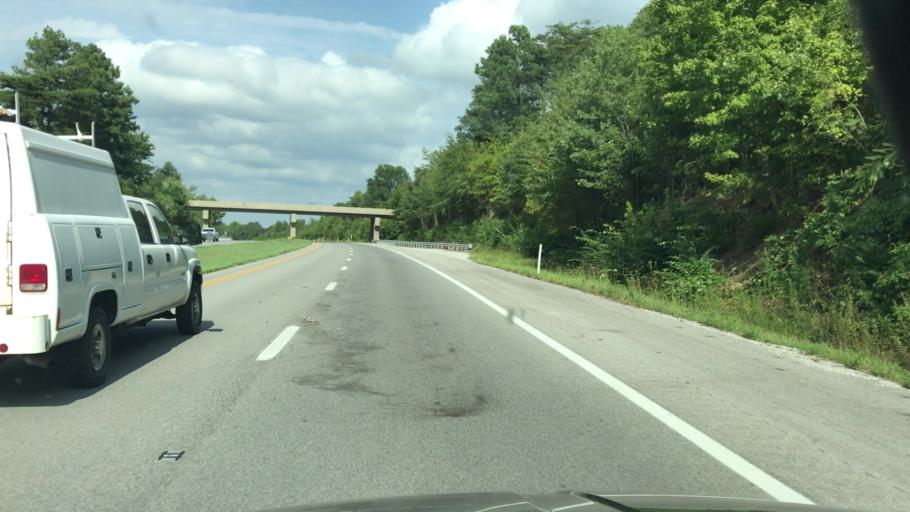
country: US
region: Kentucky
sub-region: Hopkins County
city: Dawson Springs
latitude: 37.1698
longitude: -87.7440
